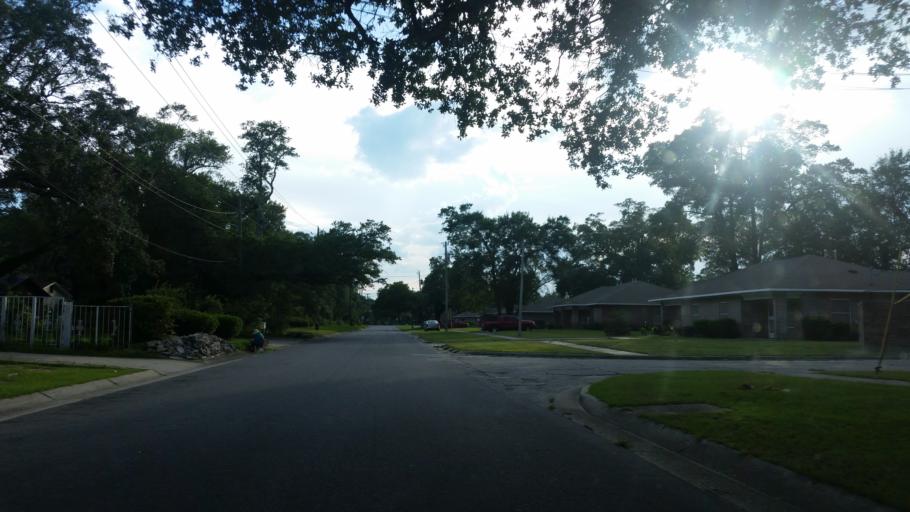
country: US
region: Florida
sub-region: Escambia County
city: Goulding
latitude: 30.4424
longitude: -87.2089
